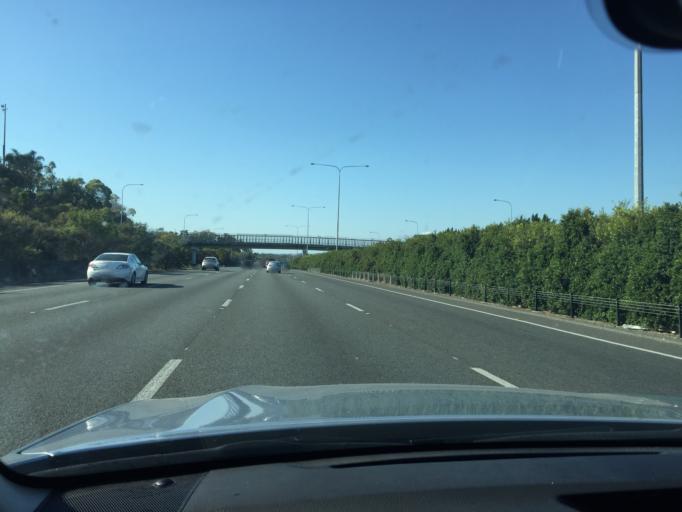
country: AU
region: Queensland
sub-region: Logan
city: Beenleigh
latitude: -27.7076
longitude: 153.2049
